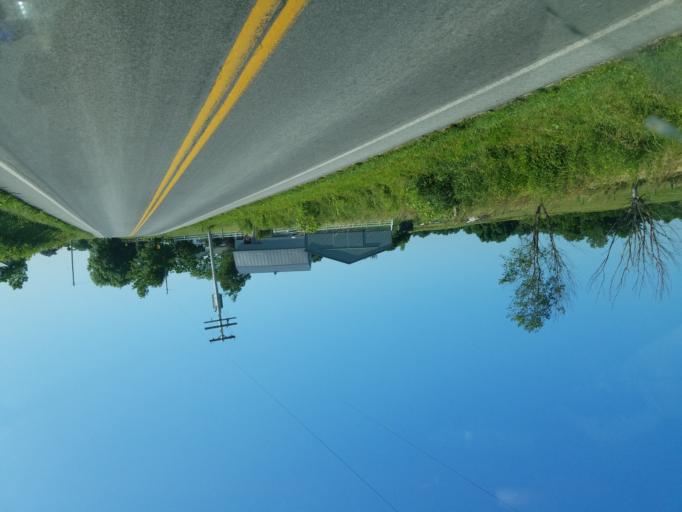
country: US
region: New York
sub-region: Wayne County
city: Clyde
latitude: 43.0420
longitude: -76.9035
